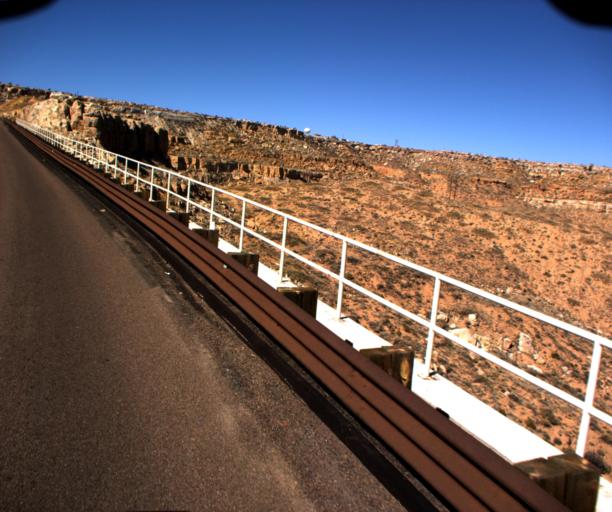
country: US
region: Arizona
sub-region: Navajo County
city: First Mesa
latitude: 35.8093
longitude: -110.5227
